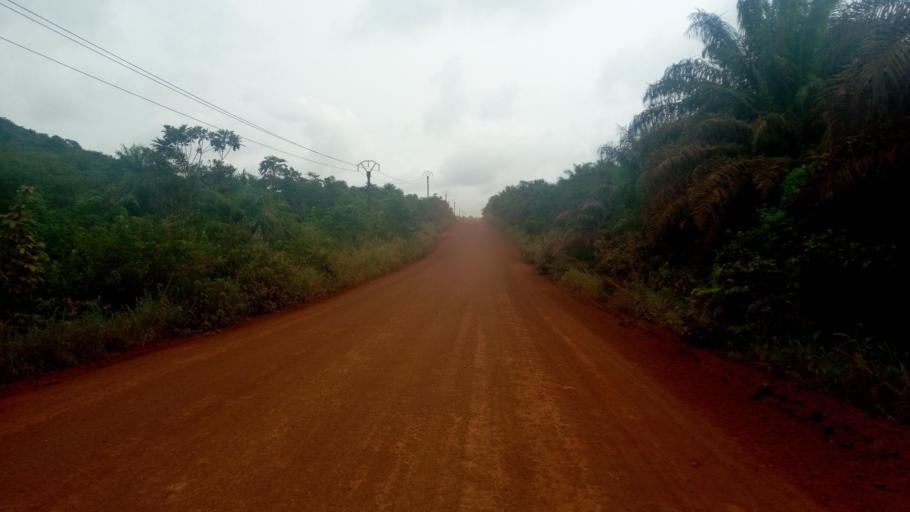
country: SL
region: Southern Province
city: Mogbwemo
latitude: 7.7110
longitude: -12.2850
